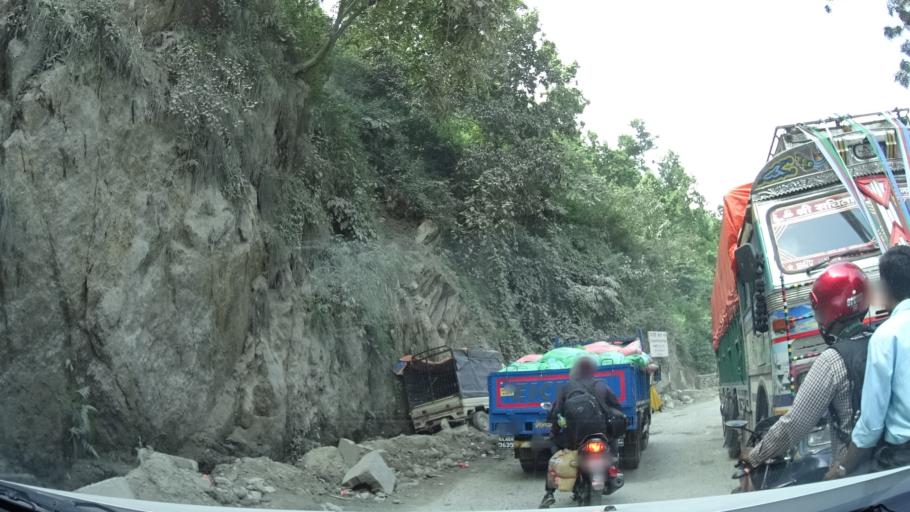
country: NP
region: Central Region
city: Kirtipur
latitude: 27.8062
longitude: 84.9686
